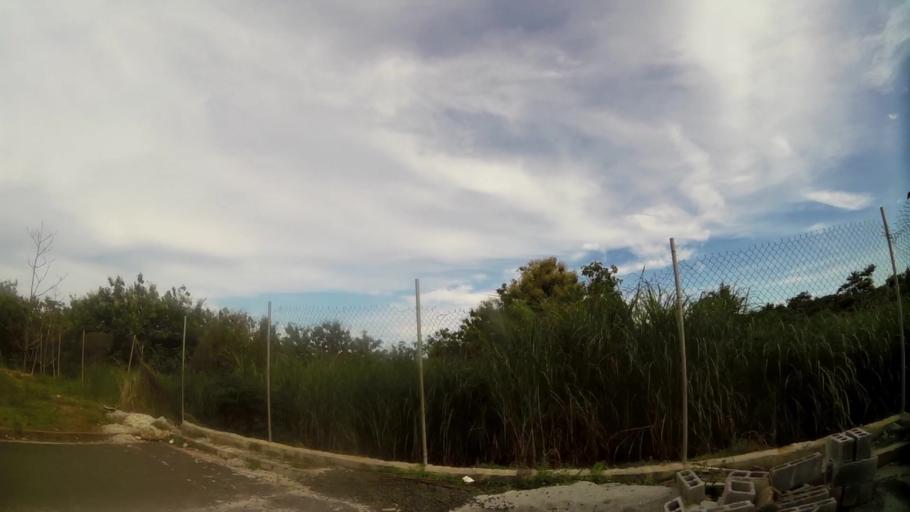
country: PA
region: Panama
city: La Chorrera
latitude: 8.8864
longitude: -79.7558
